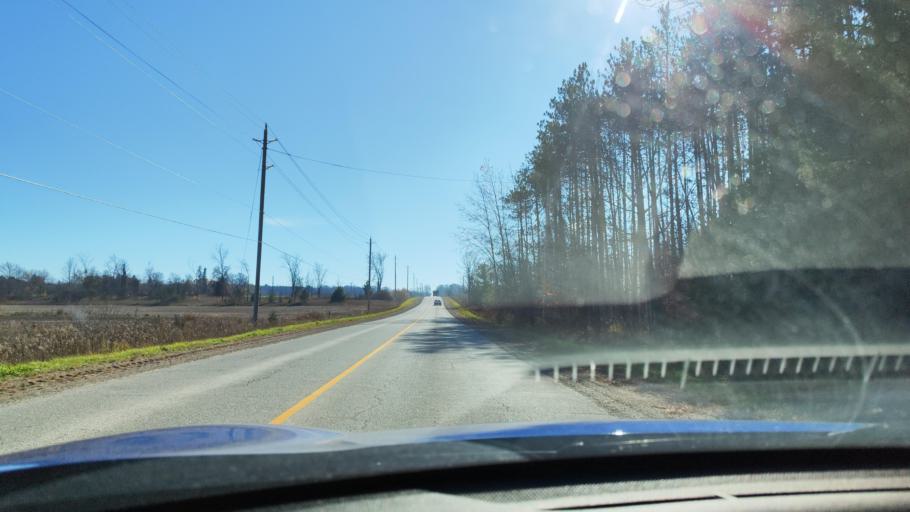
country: CA
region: Ontario
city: Wasaga Beach
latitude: 44.4646
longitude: -80.0044
